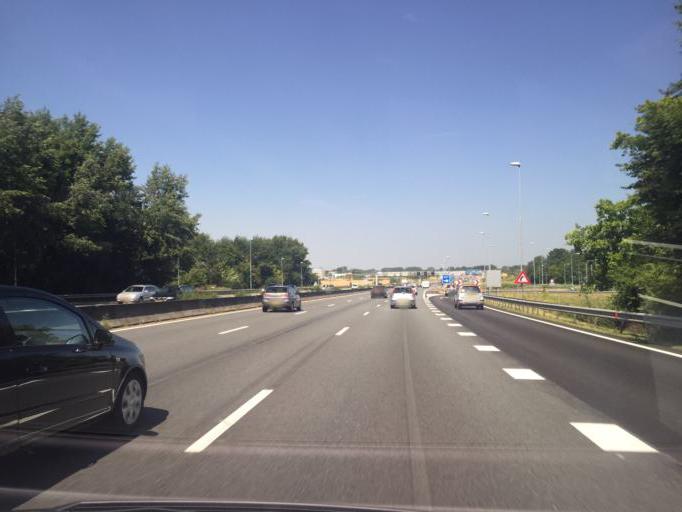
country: NL
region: North Holland
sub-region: Gemeente Amstelveen
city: Amstelveen
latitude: 52.3141
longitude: 4.8136
